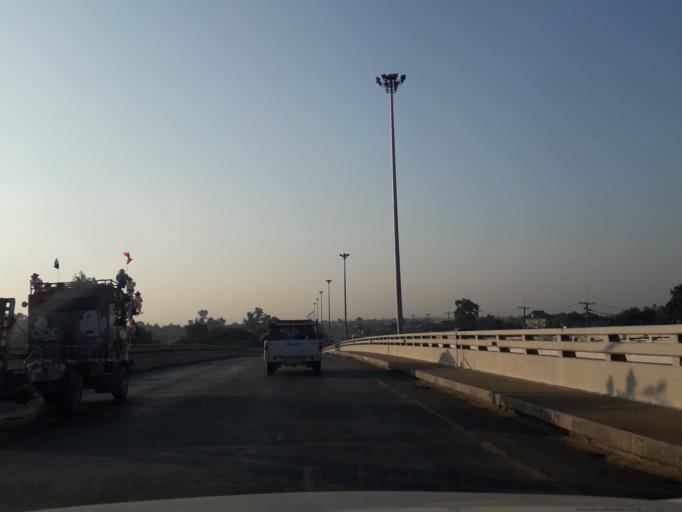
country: TH
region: Phra Nakhon Si Ayutthaya
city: Bang Pa-in
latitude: 14.1938
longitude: 100.5529
